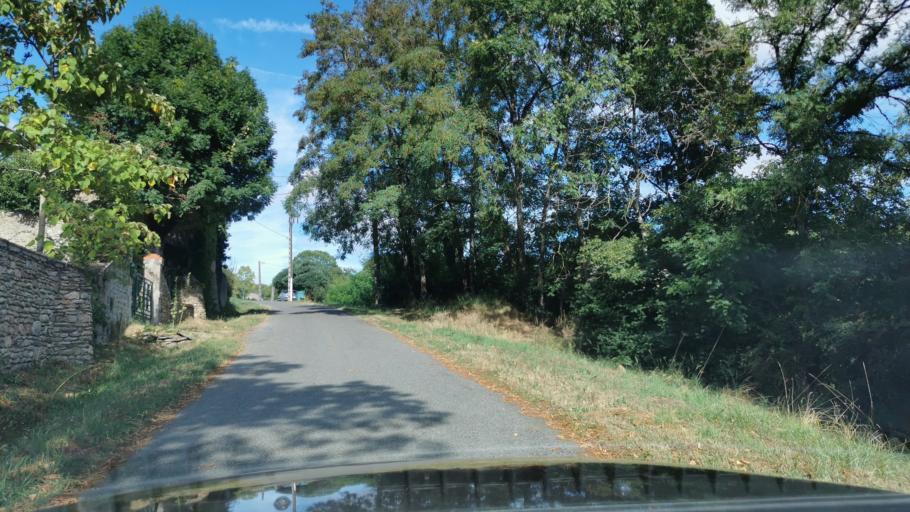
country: FR
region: Bourgogne
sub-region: Departement de Saone-et-Loire
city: Marmagne
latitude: 46.8721
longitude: 4.3368
